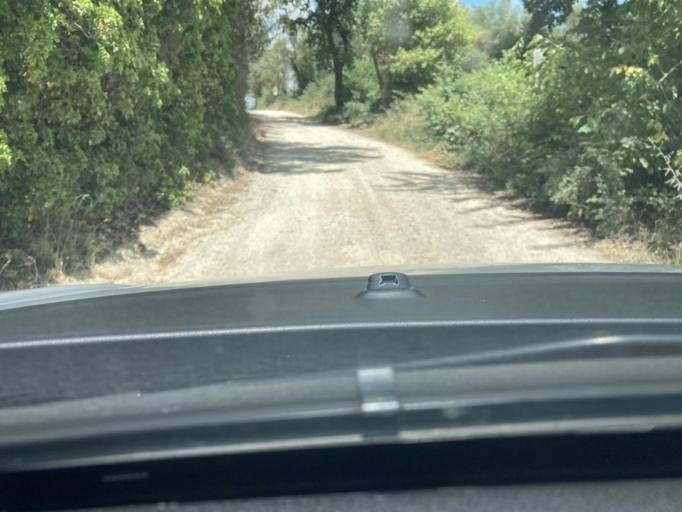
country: IT
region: Umbria
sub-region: Provincia di Perugia
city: Corciano
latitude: 43.1284
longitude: 12.2636
